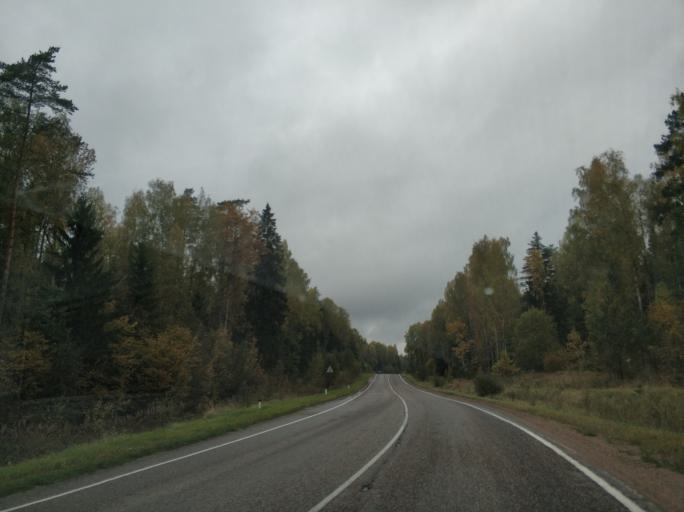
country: RU
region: Pskov
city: Opochka
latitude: 56.5176
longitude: 28.6607
